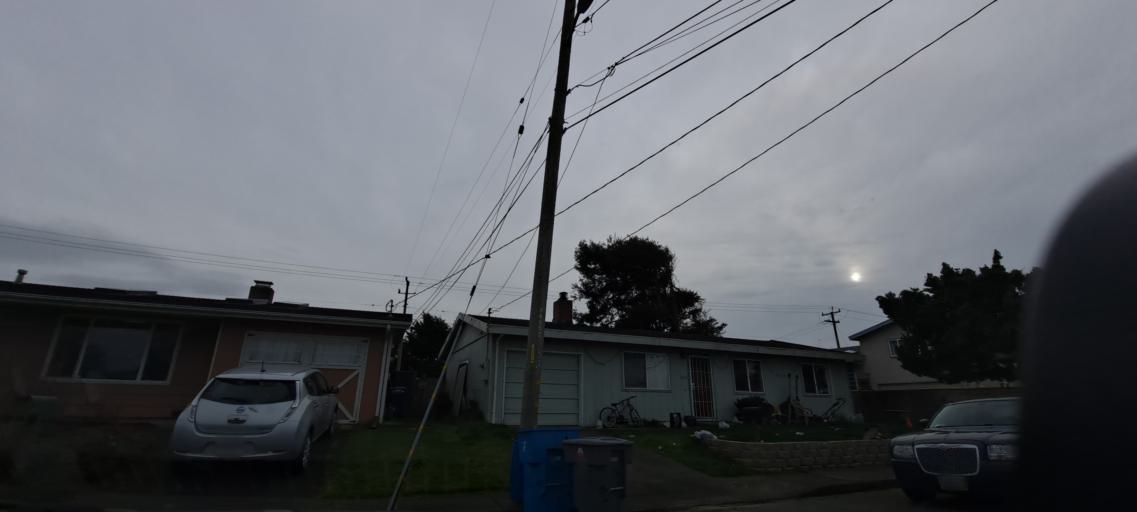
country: US
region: California
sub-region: Humboldt County
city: Arcata
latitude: 40.8725
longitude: -124.1054
